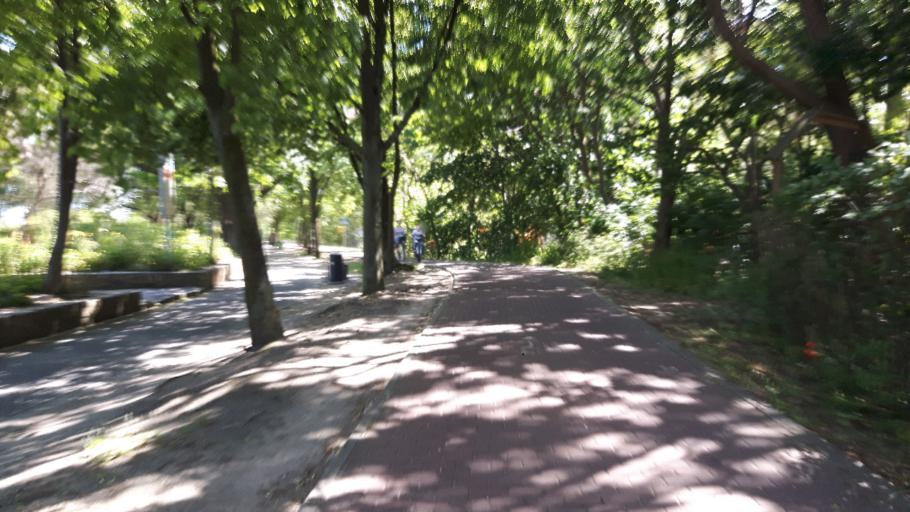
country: PL
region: Pomeranian Voivodeship
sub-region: Sopot
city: Sopot
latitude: 54.4313
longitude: 18.5883
